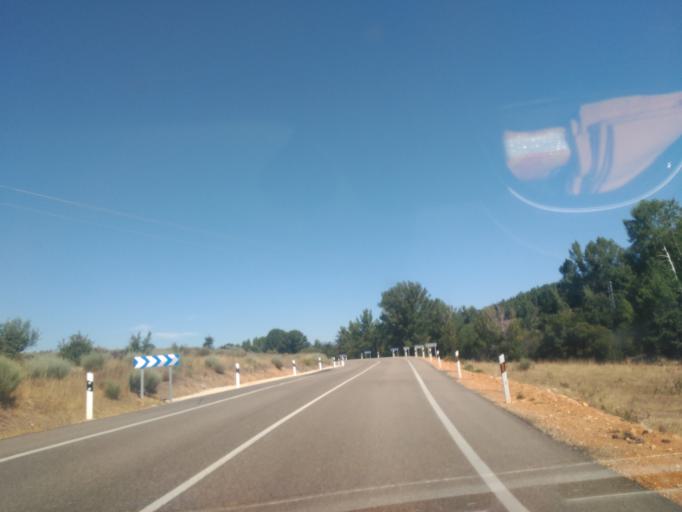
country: ES
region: Castille and Leon
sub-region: Provincia de Zamora
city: Ferreras de Arriba
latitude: 41.9582
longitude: -6.2156
